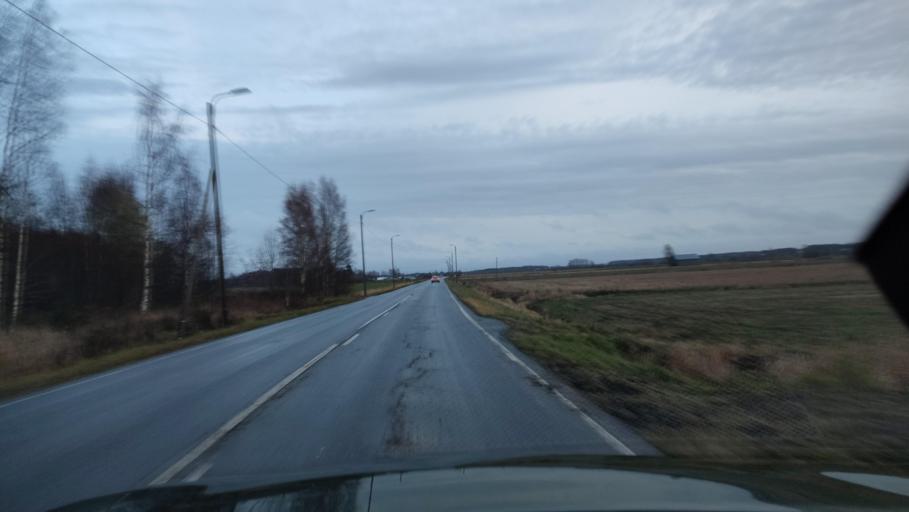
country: FI
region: Ostrobothnia
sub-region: Vaasa
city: Ristinummi
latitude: 63.0478
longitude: 21.7402
